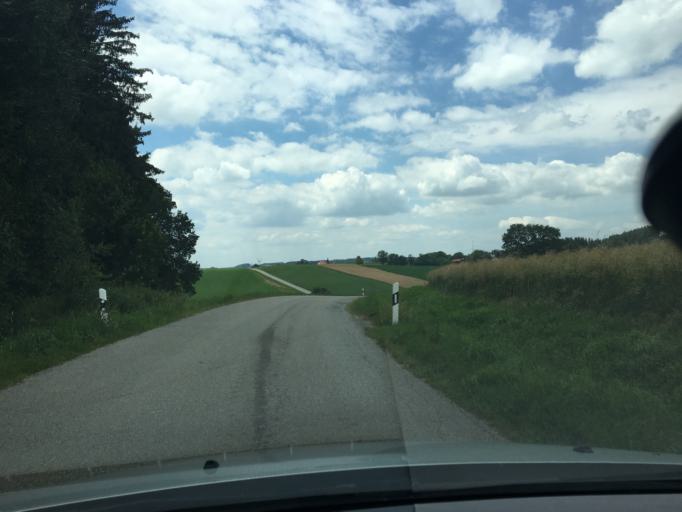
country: DE
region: Bavaria
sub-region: Upper Bavaria
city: Egglkofen
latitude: 48.3936
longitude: 12.4656
